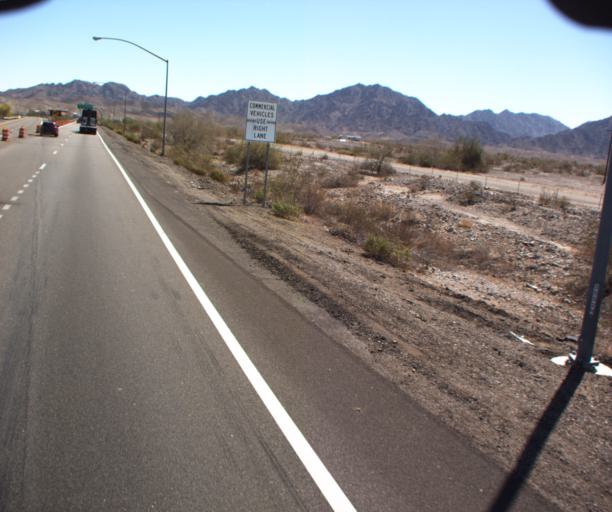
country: US
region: Arizona
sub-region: Yuma County
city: Fortuna Foothills
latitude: 32.6604
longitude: -114.3711
